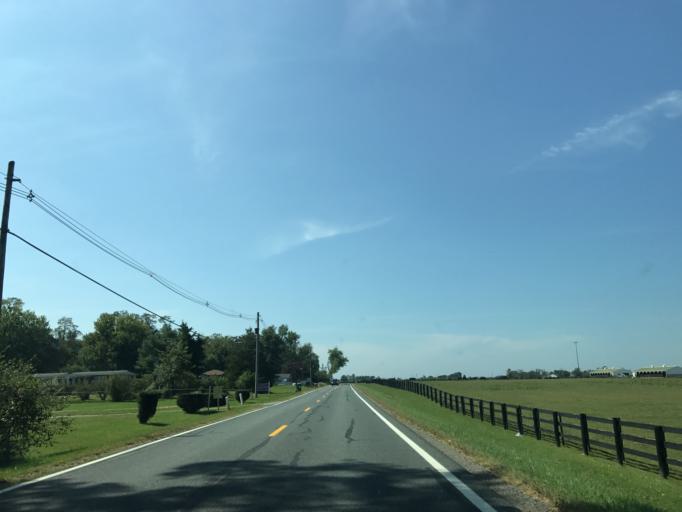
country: US
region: Maryland
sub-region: Cecil County
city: Elkton
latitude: 39.4904
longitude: -75.8321
